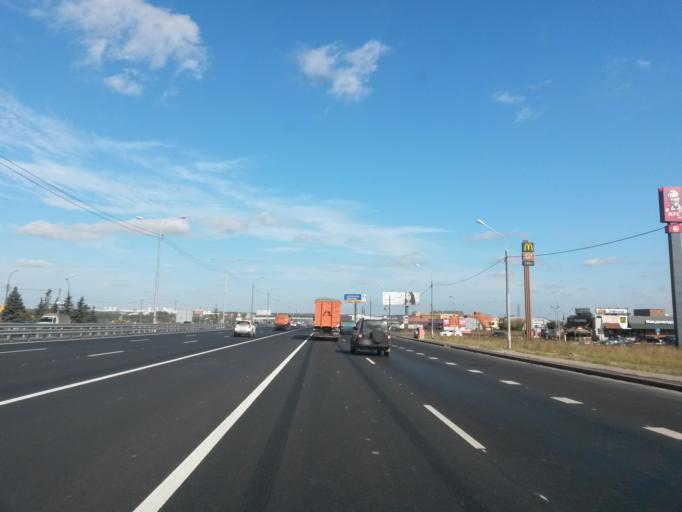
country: RU
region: Moskovskaya
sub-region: Podol'skiy Rayon
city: Podol'sk
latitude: 55.4442
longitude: 37.6171
